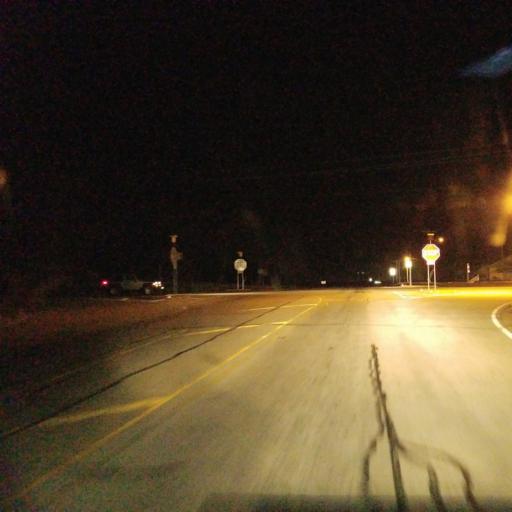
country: US
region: Illinois
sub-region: Knox County
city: Abingdon
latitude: 40.7291
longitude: -90.4053
